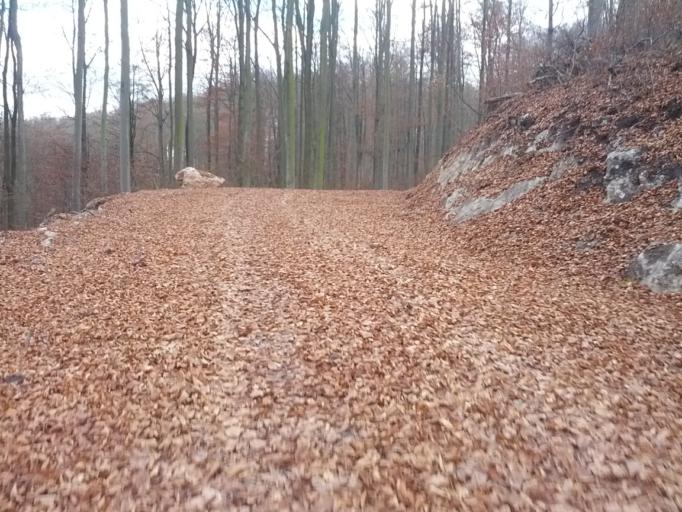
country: DE
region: Thuringia
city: Krauthausen
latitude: 50.9759
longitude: 10.2356
